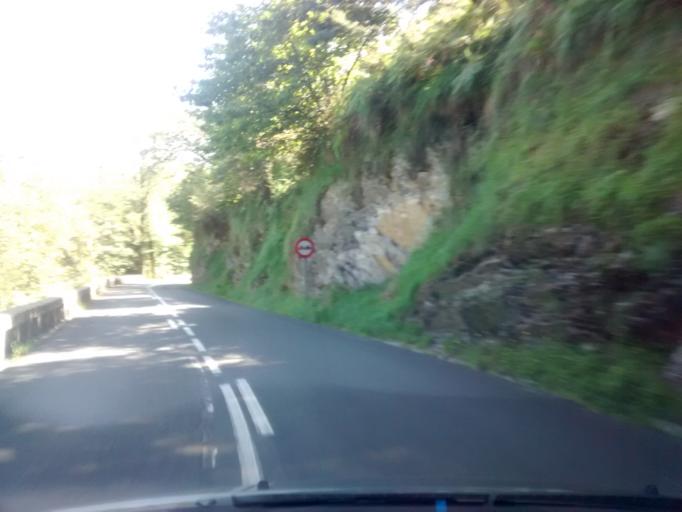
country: ES
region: Basque Country
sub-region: Provincia de Guipuzcoa
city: Eibar
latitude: 43.1982
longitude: -2.4758
